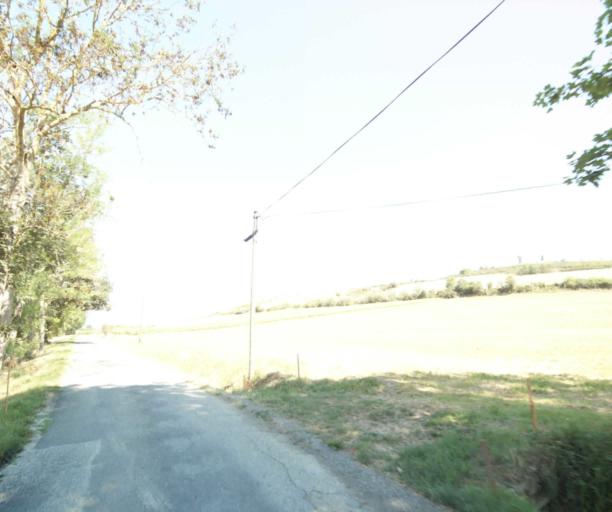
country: FR
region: Midi-Pyrenees
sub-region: Departement de l'Ariege
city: Lezat-sur-Leze
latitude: 43.2684
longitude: 1.3615
